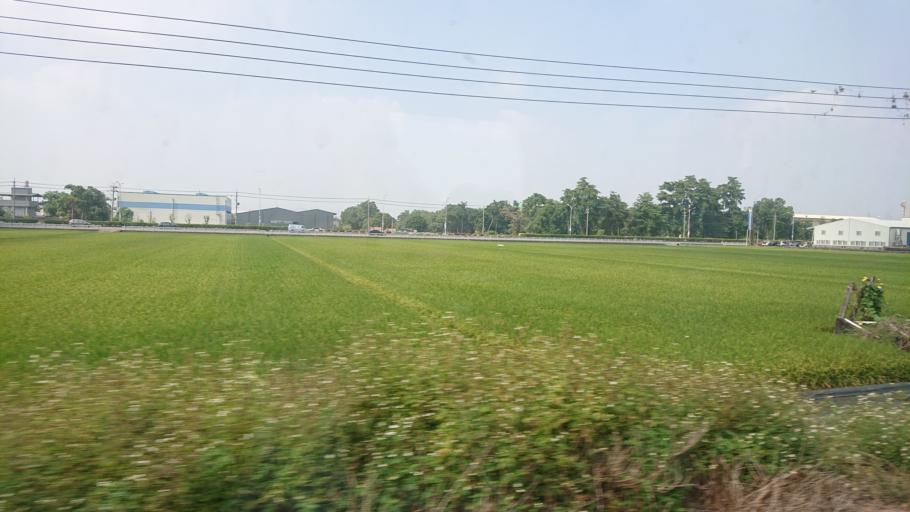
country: TW
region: Taiwan
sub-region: Yunlin
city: Douliu
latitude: 23.6361
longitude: 120.4703
